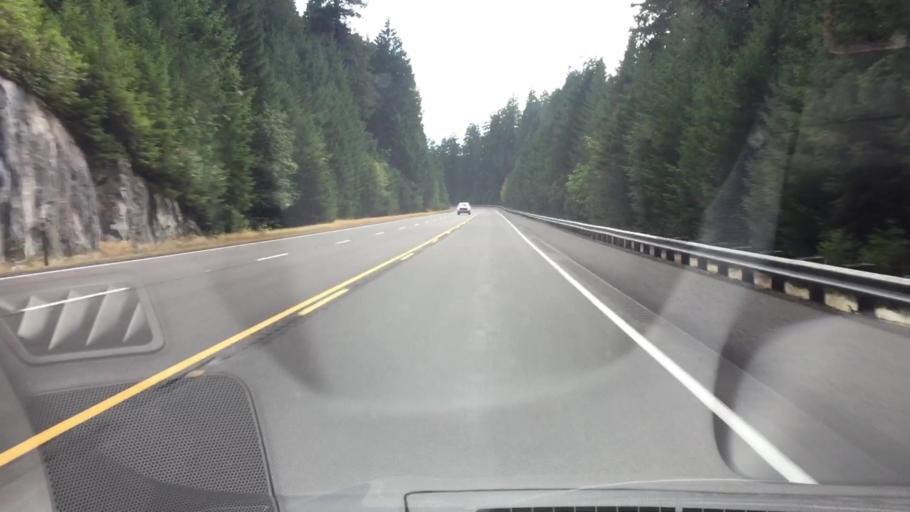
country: US
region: Washington
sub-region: Pierce County
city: Buckley
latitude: 46.6635
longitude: -121.5974
